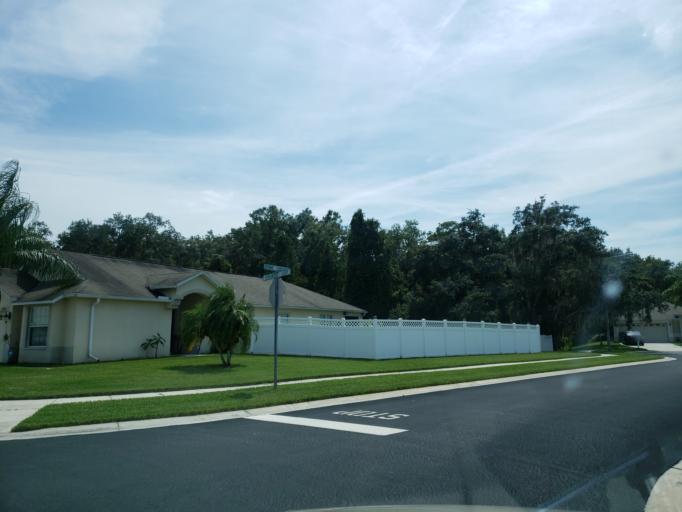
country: US
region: Florida
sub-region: Pasco County
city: Wesley Chapel
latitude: 28.2227
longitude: -82.3883
